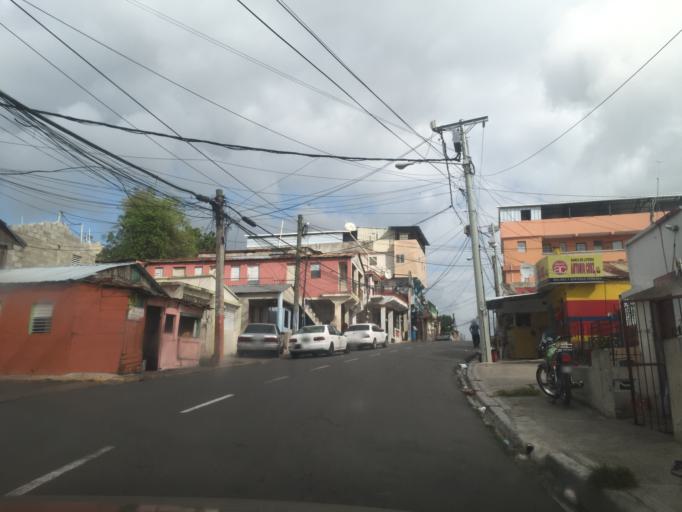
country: DO
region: Santiago
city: Santiago de los Caballeros
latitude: 19.4234
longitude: -70.7161
